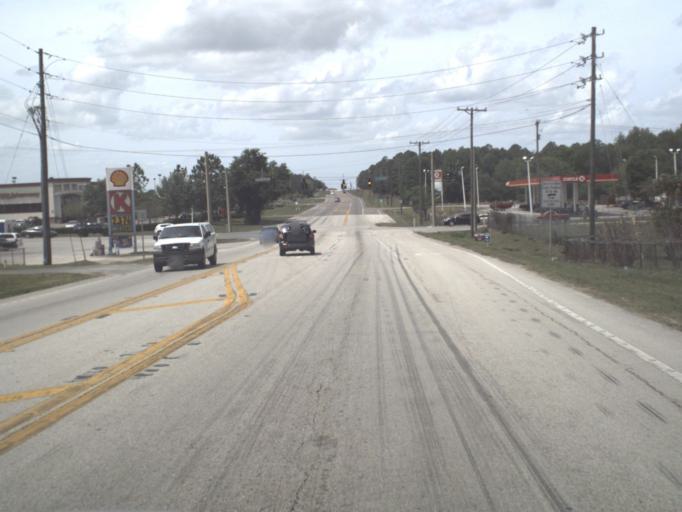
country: US
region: Florida
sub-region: Lake County
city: Mount Plymouth
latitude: 28.8516
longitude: -81.5502
